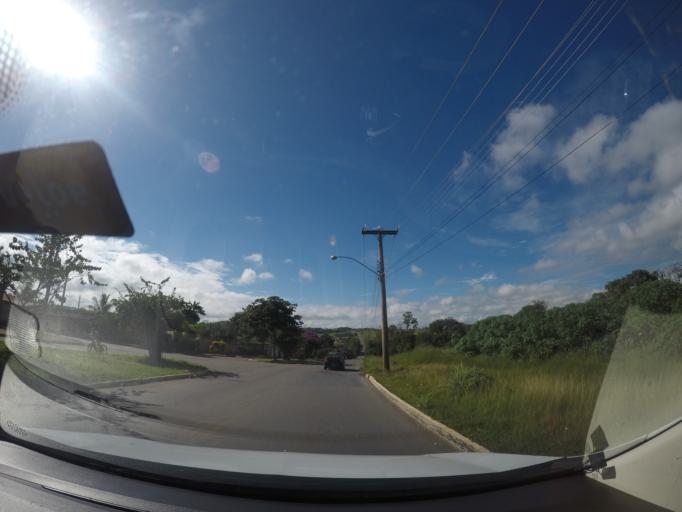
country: BR
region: Goias
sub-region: Senador Canedo
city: Senador Canedo
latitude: -16.6569
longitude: -49.1539
